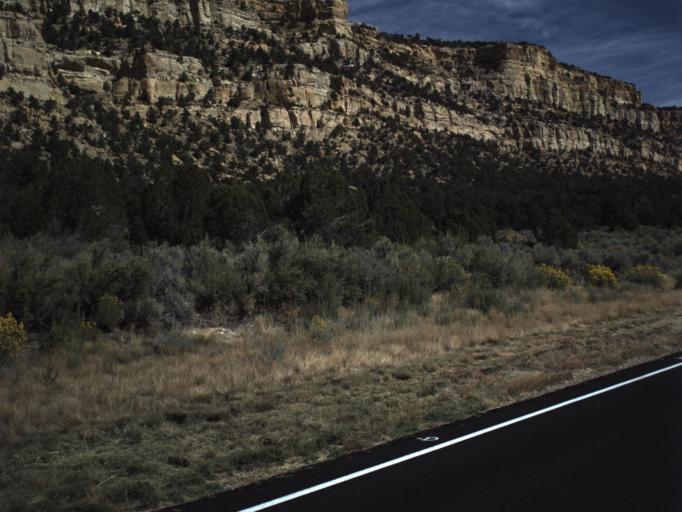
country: US
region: Utah
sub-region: Garfield County
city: Panguitch
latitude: 37.7274
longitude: -111.7704
